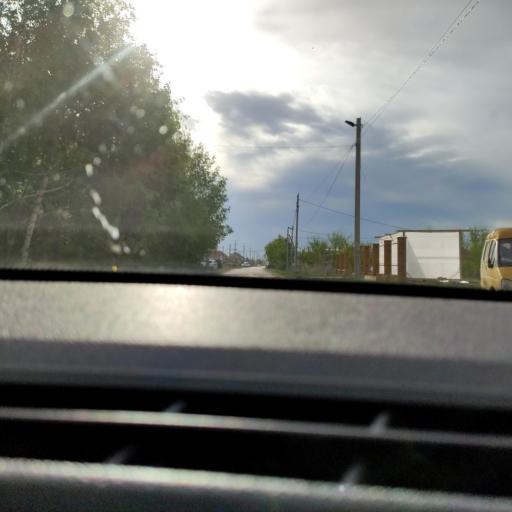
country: RU
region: Samara
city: Tol'yatti
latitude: 53.5552
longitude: 49.4042
